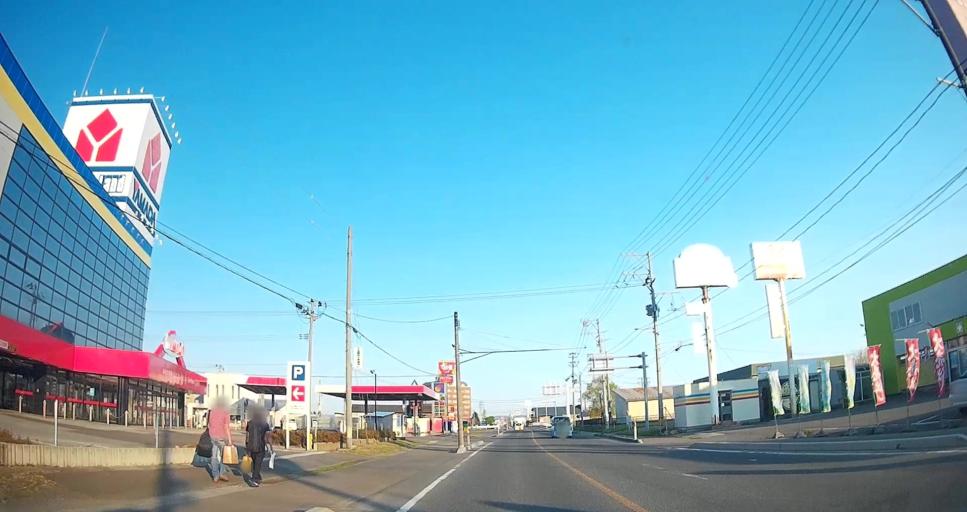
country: JP
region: Aomori
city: Mutsu
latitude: 41.2867
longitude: 141.1861
